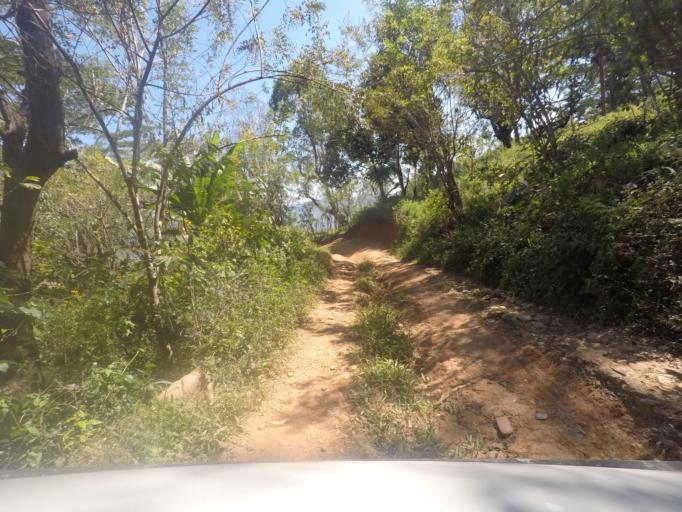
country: TL
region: Ermera
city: Gleno
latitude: -8.7191
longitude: 125.3192
